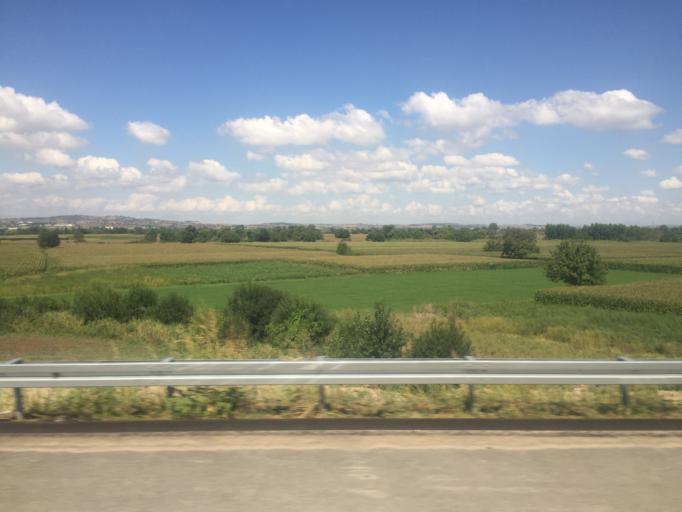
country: TR
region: Balikesir
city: Gobel
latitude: 40.0222
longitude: 28.2060
